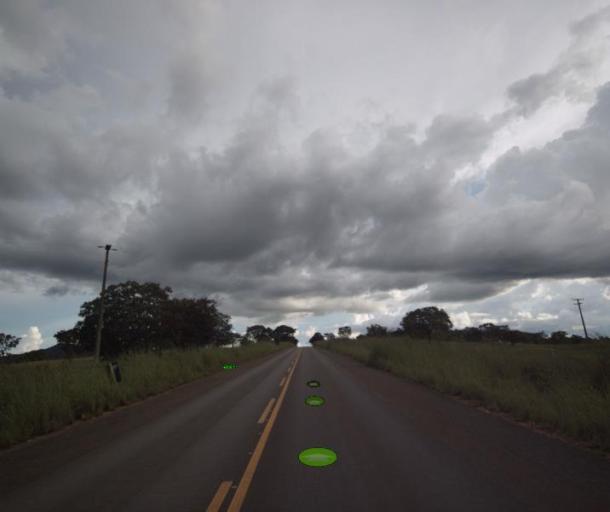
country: BR
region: Goias
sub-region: Niquelandia
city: Niquelandia
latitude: -14.4913
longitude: -48.4905
